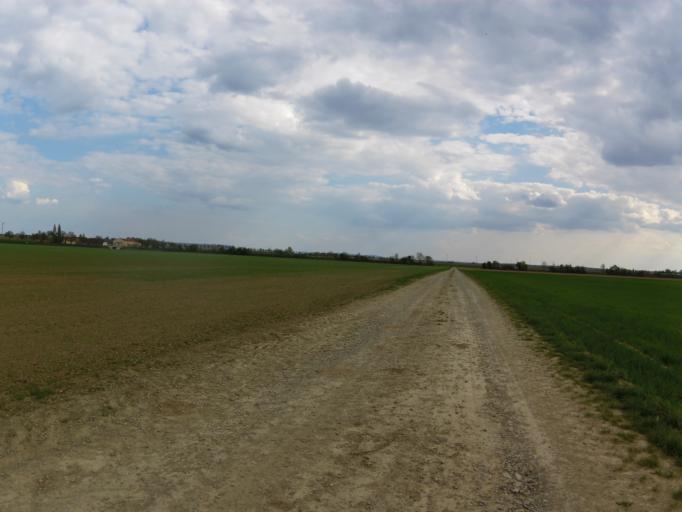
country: DE
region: Bavaria
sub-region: Regierungsbezirk Unterfranken
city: Oberpleichfeld
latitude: 49.8470
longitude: 10.0960
